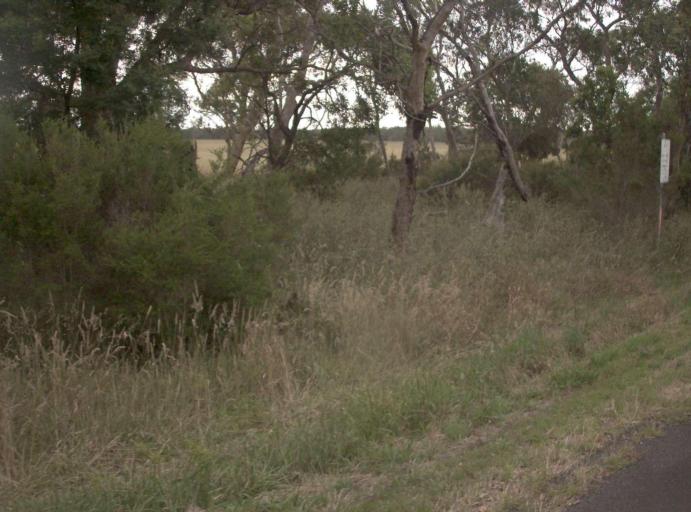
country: AU
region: Victoria
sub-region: Latrobe
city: Traralgon
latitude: -38.5507
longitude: 146.8221
